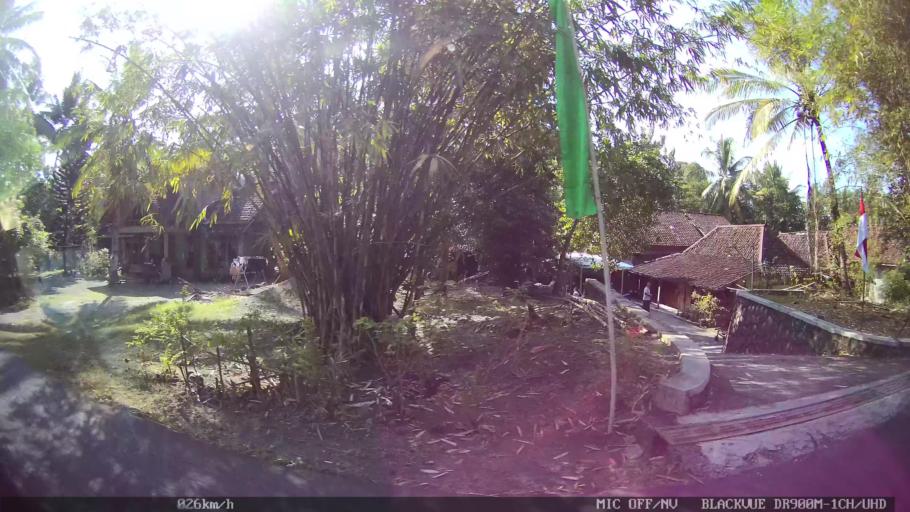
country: ID
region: Daerah Istimewa Yogyakarta
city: Kasihan
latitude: -7.8260
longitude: 110.2891
